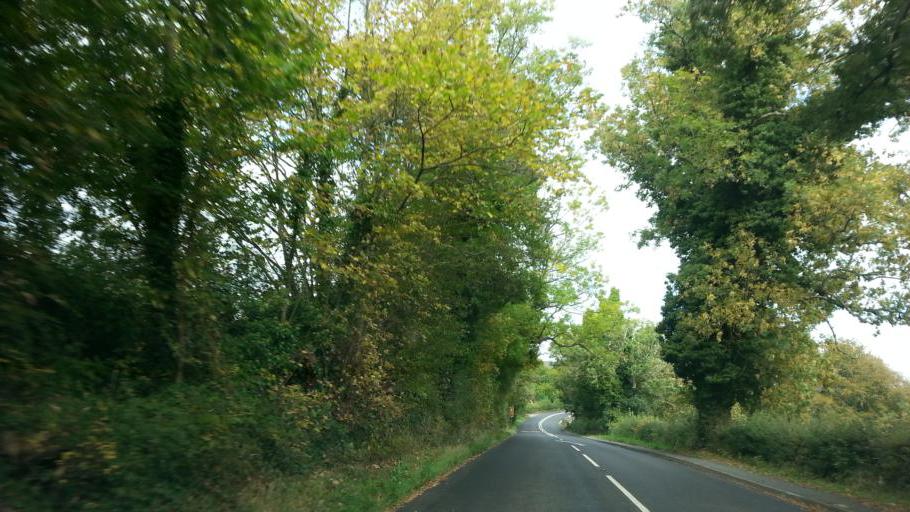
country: GB
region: England
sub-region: Gloucestershire
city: Painswick
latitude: 51.7725
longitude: -2.2133
